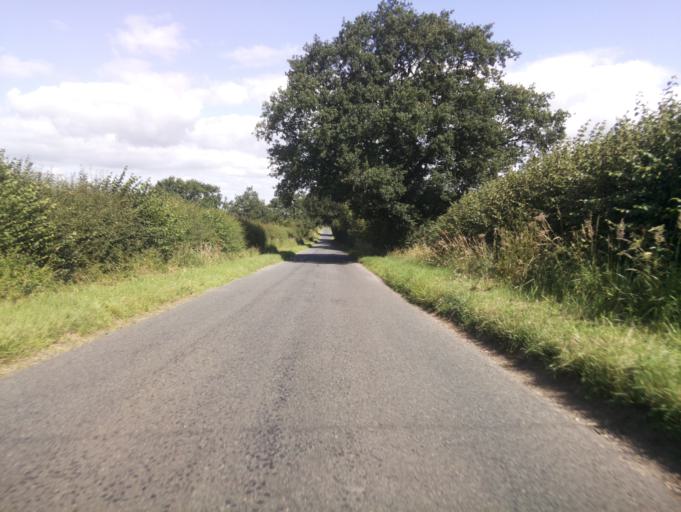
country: GB
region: England
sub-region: Milton Keynes
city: Calverton
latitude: 51.9897
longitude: -0.8573
